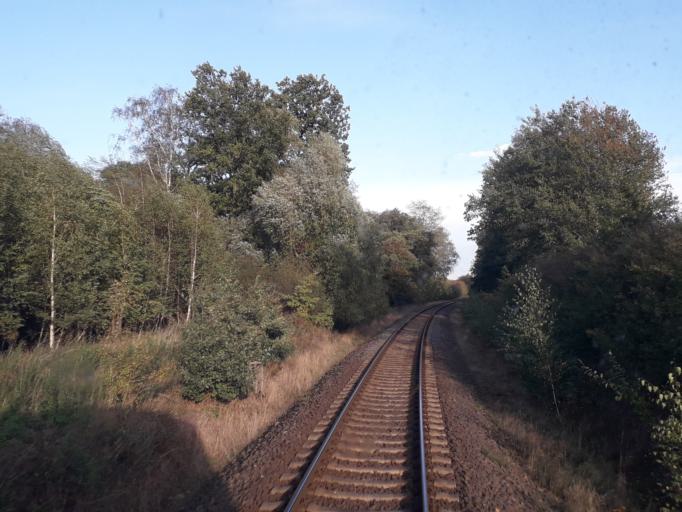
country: DE
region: Brandenburg
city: Pritzwalk
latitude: 53.1433
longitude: 12.1348
